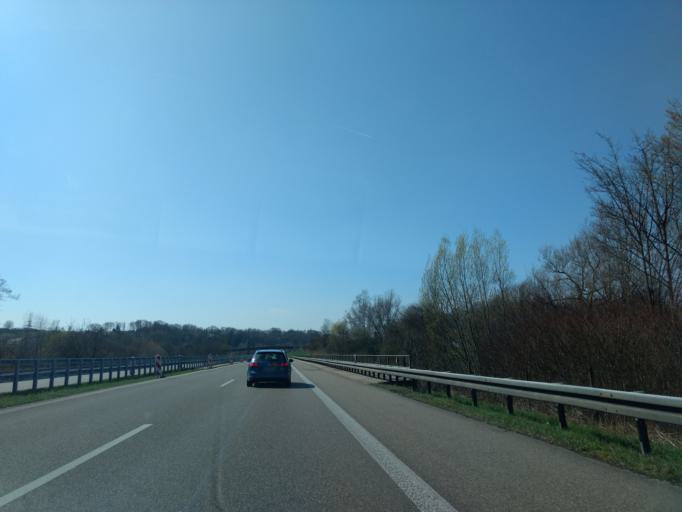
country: DE
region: Baden-Wuerttemberg
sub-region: Regierungsbezirk Stuttgart
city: Reichenbach an der Fils
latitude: 48.7089
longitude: 9.4831
